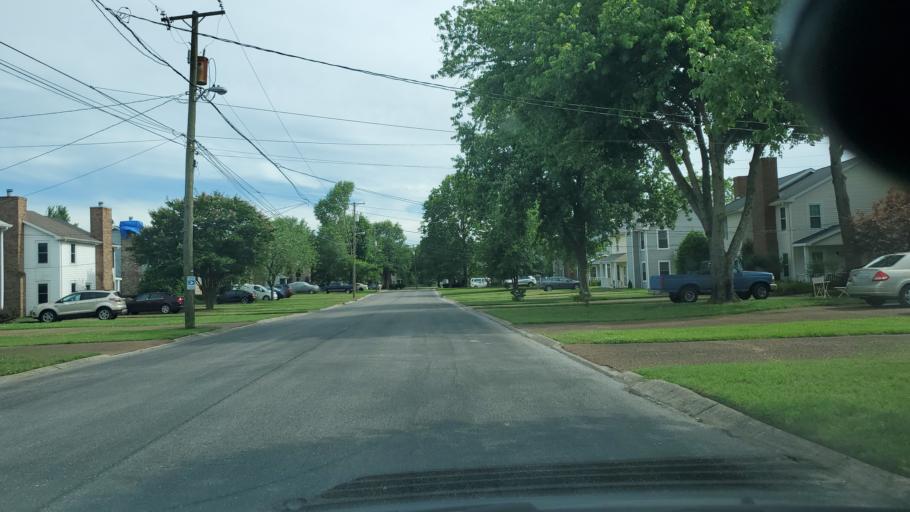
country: US
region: Tennessee
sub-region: Davidson County
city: Lakewood
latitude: 36.2081
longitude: -86.6875
